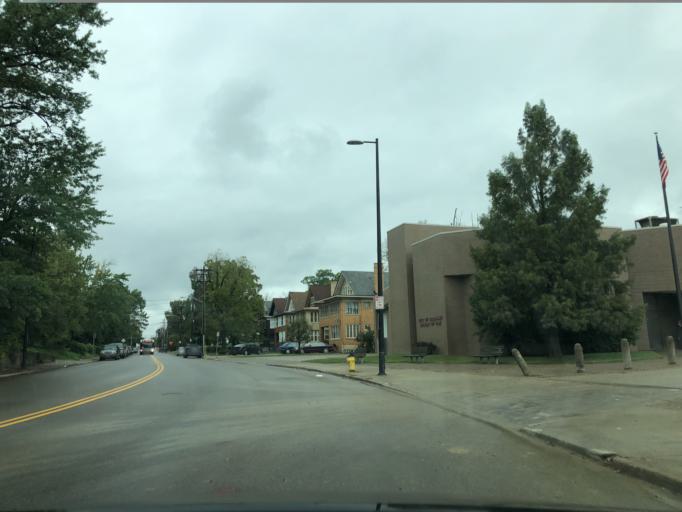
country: US
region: Ohio
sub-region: Hamilton County
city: Saint Bernard
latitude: 39.1456
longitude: -84.4922
